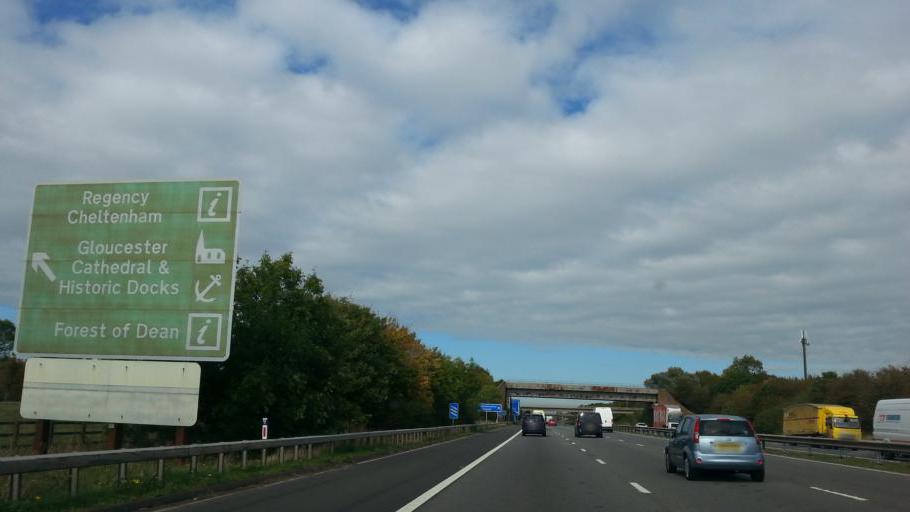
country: GB
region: England
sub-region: Gloucestershire
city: Churchdown
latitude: 51.8814
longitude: -2.1512
